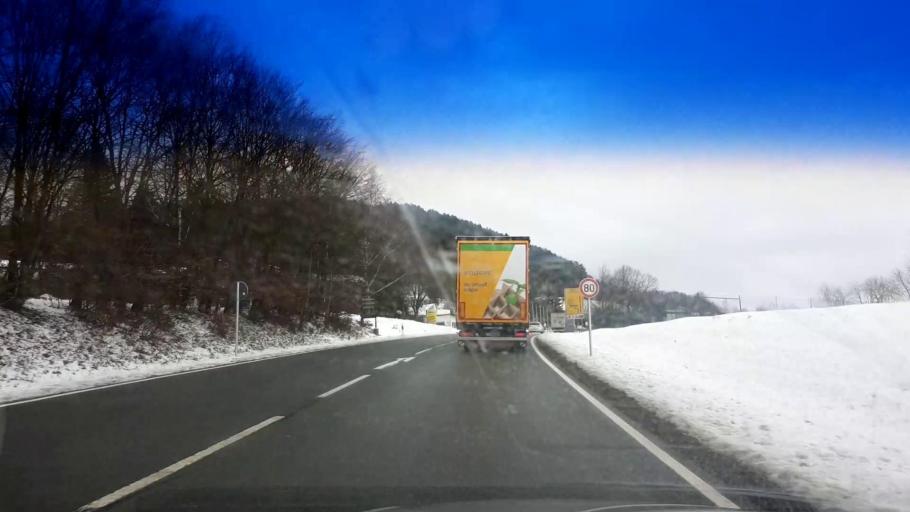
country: DE
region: Bavaria
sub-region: Upper Palatinate
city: Kemnath
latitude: 49.8666
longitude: 11.9478
